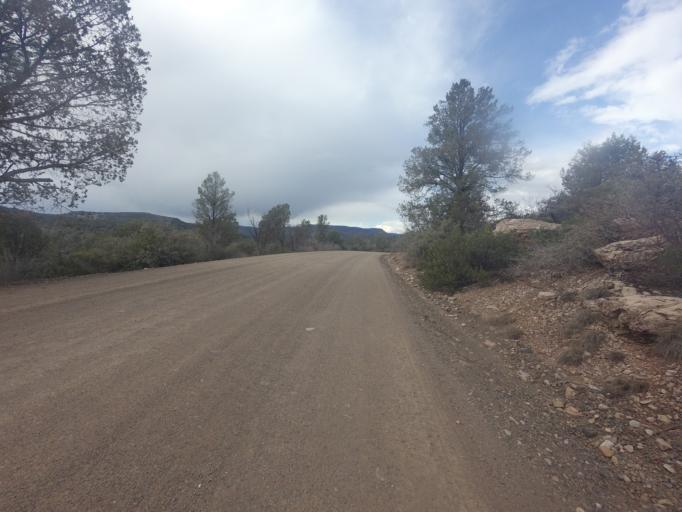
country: US
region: Arizona
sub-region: Gila County
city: Payson
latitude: 34.2968
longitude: -111.3542
